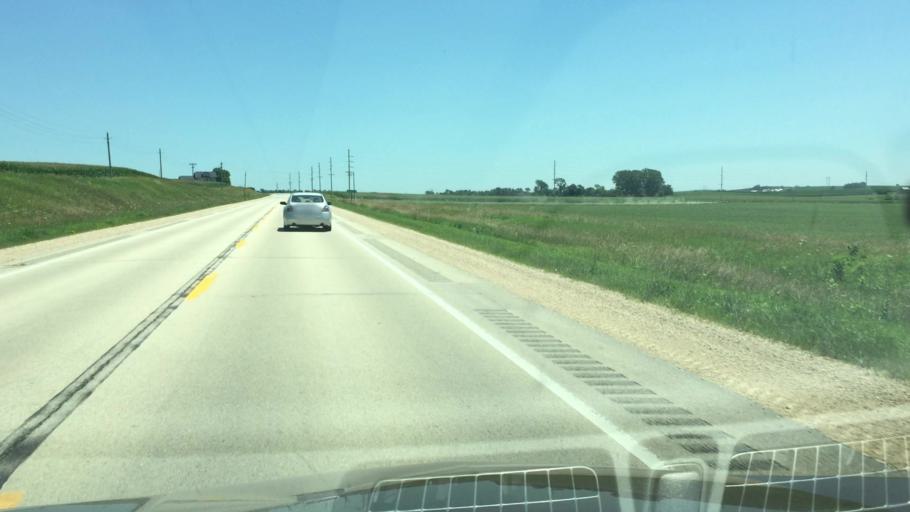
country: US
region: Iowa
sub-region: Jackson County
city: Maquoketa
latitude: 42.0681
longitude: -90.7856
